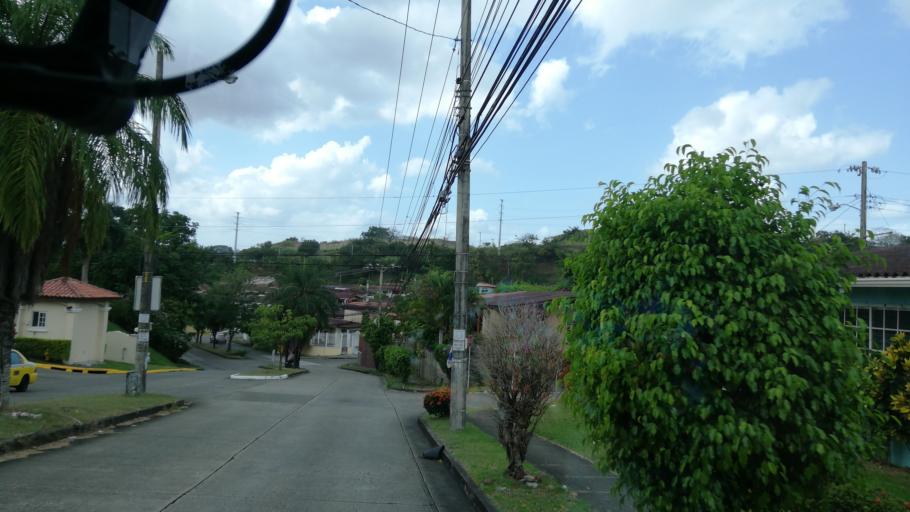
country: PA
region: Panama
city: San Miguelito
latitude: 9.0640
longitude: -79.4591
